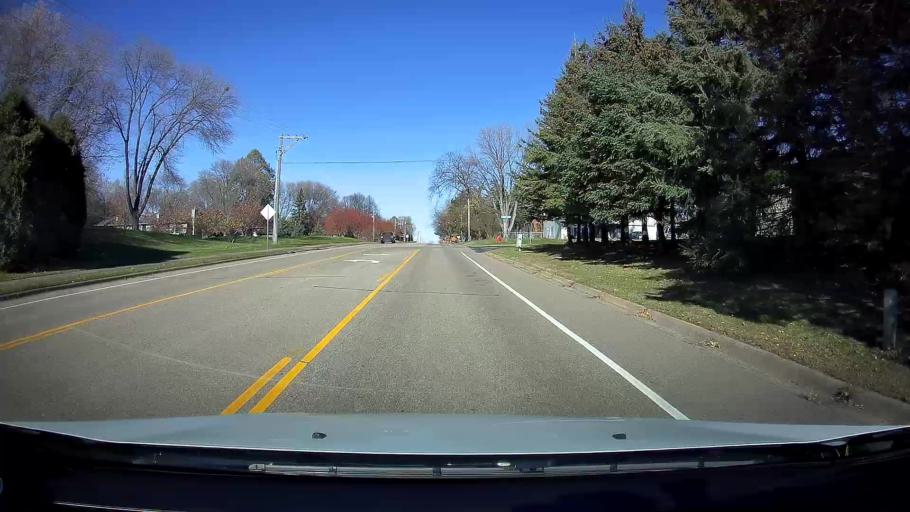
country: US
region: Minnesota
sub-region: Ramsey County
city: Shoreview
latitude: 45.0730
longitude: -93.1575
